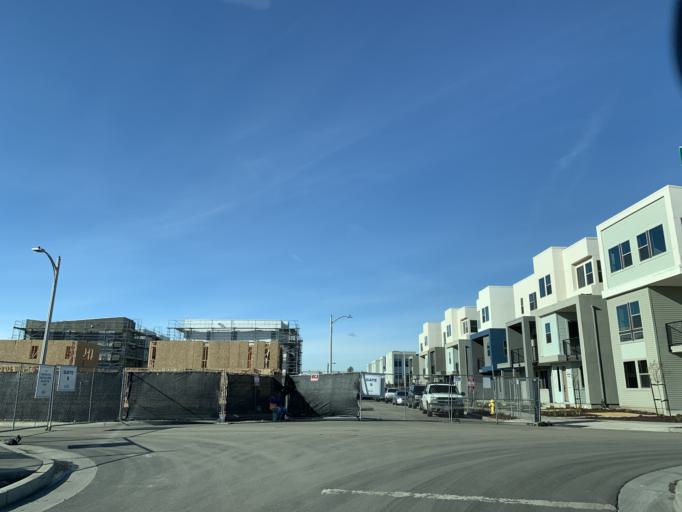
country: US
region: California
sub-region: Santa Clara County
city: Seven Trees
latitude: 37.2416
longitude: -121.7867
